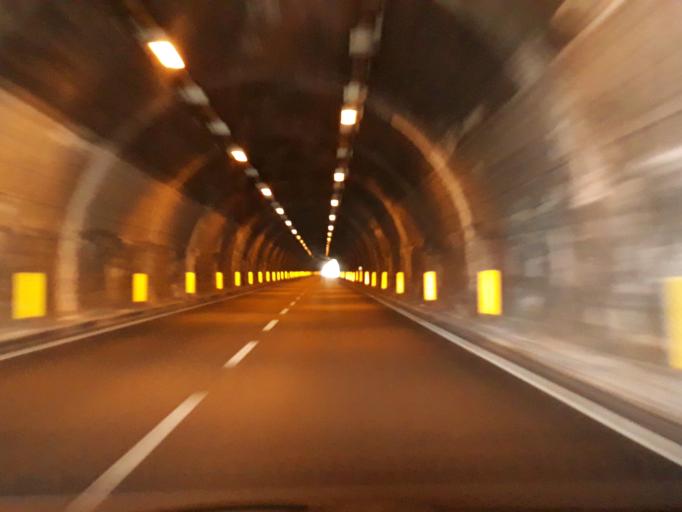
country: IT
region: Sicily
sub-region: Palermo
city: Trabia
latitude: 37.9940
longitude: 13.6501
